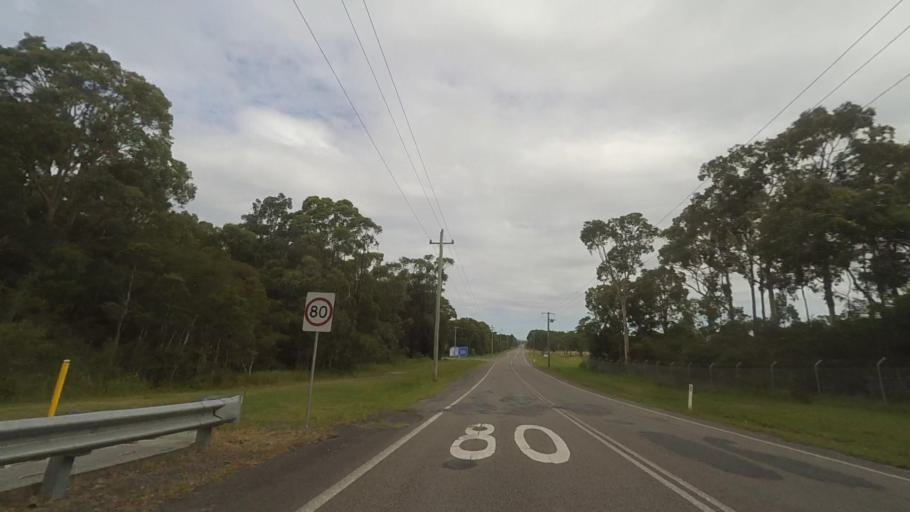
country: AU
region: New South Wales
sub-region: Great Lakes
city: Hawks Nest
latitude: -32.6425
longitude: 152.1458
